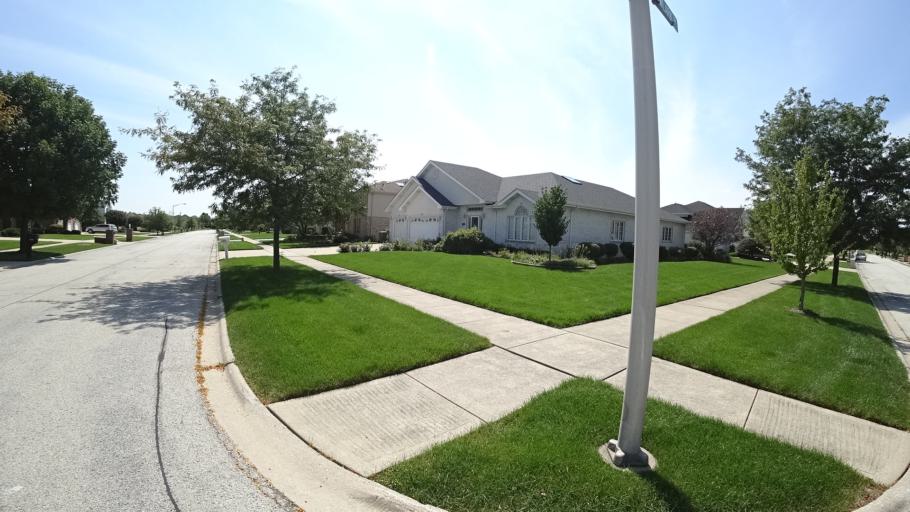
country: US
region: Illinois
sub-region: Cook County
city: Orland Hills
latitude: 41.5646
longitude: -87.8328
